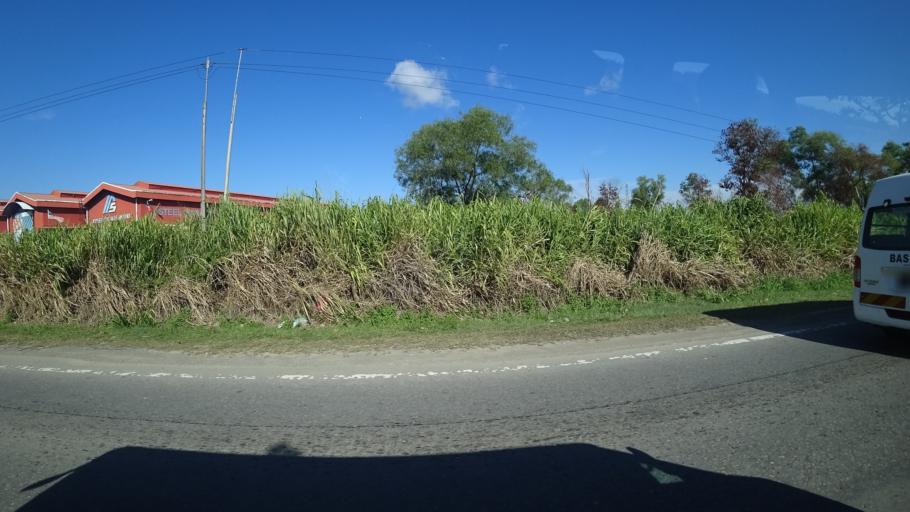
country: MY
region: Sabah
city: Kota Kinabalu
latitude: 6.1045
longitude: 116.2031
